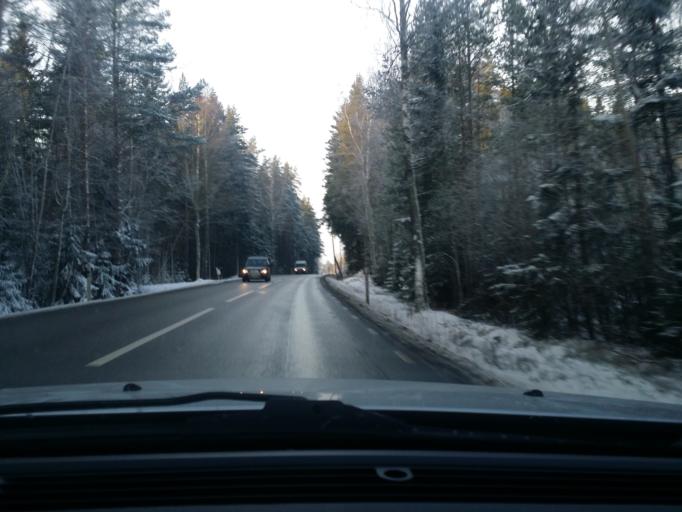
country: SE
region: OErebro
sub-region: Lindesbergs Kommun
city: Frovi
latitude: 59.5198
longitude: 15.3206
